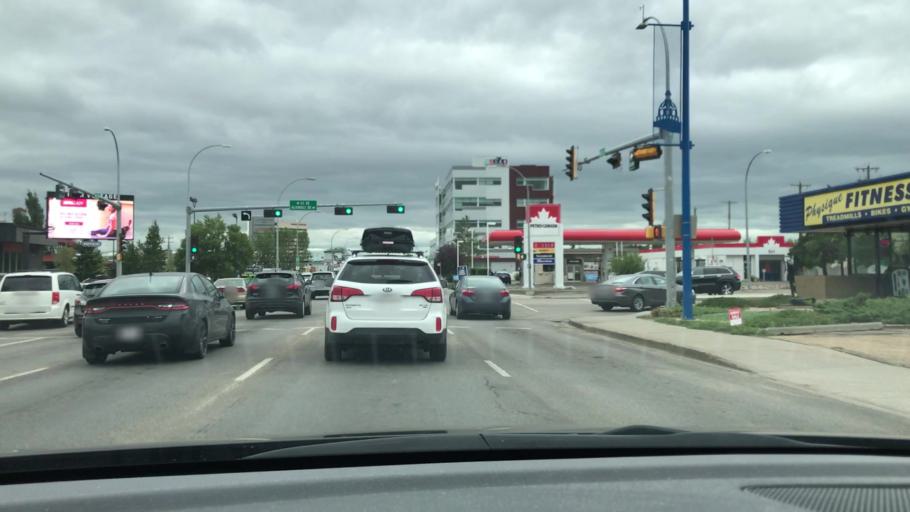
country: CA
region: Alberta
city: Edmonton
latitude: 53.5002
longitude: -113.4977
